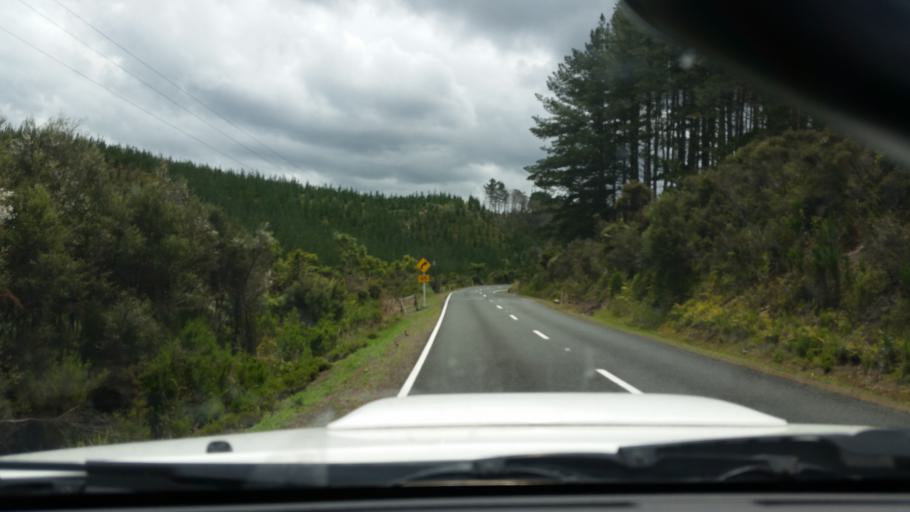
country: NZ
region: Northland
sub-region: Kaipara District
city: Dargaville
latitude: -35.8200
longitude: 173.7107
